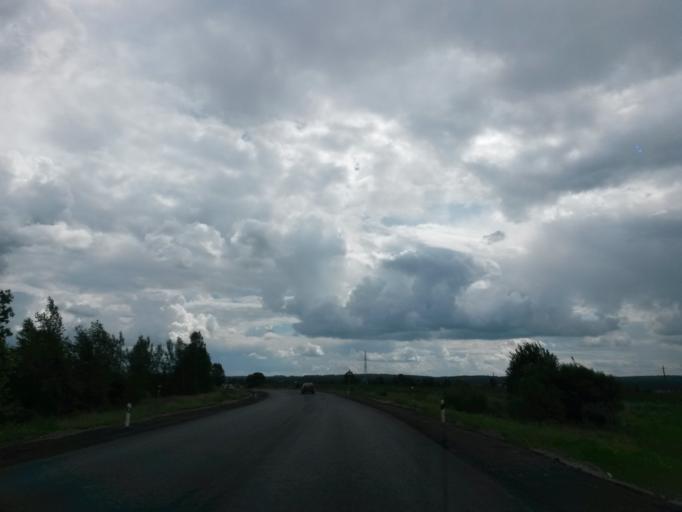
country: RU
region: Jaroslavl
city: Yaroslavl
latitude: 57.5259
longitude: 39.8799
